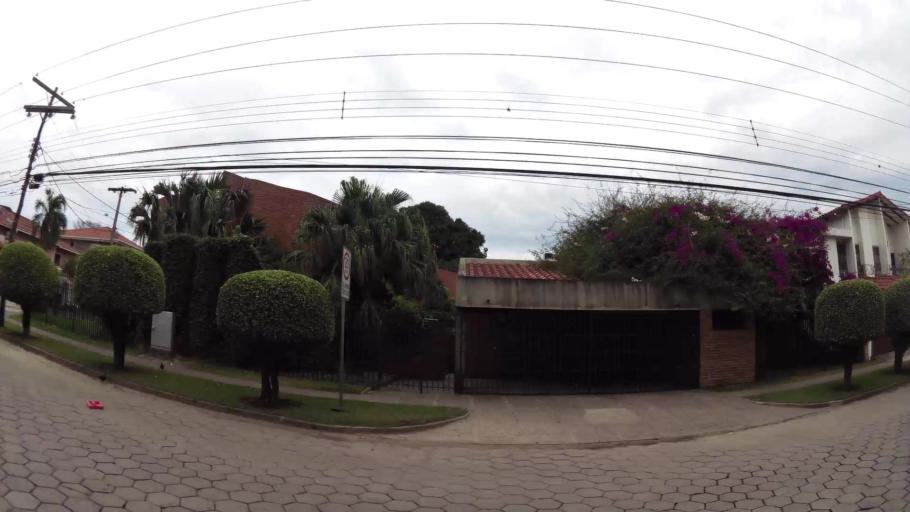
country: BO
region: Santa Cruz
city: Santa Cruz de la Sierra
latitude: -17.7642
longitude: -63.1689
